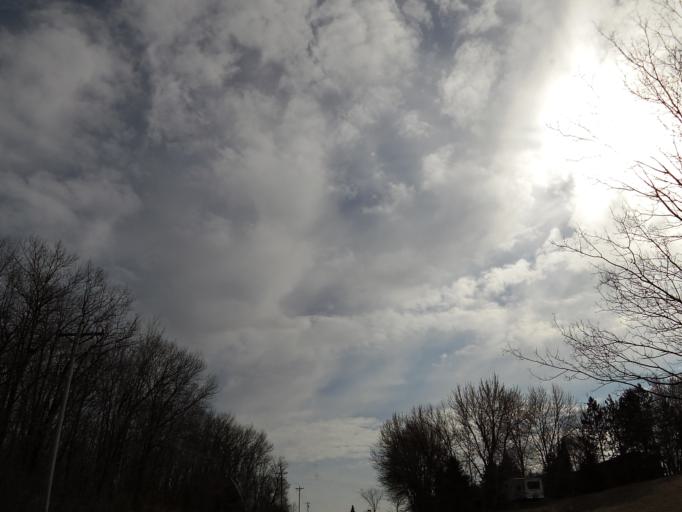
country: US
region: Minnesota
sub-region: Scott County
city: Prior Lake
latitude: 44.6831
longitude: -93.3793
